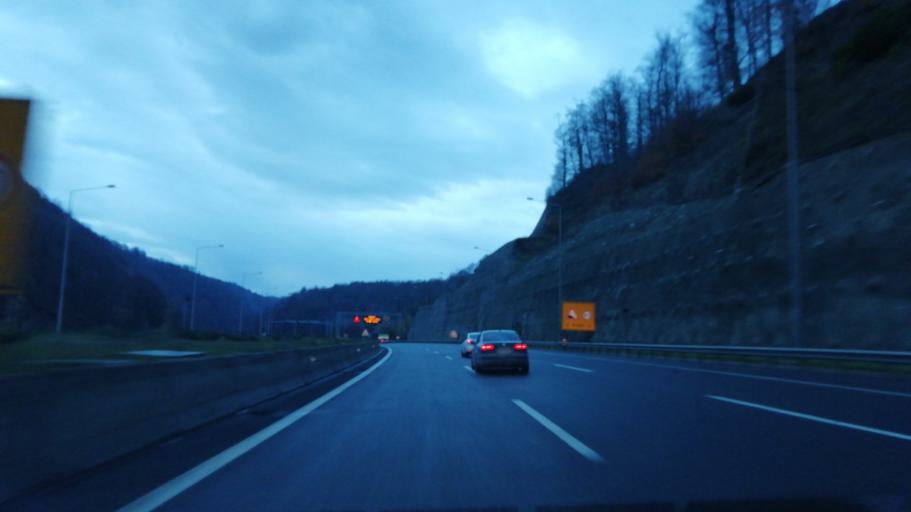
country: TR
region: Duzce
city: Kaynasli
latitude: 40.7586
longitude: 31.4469
